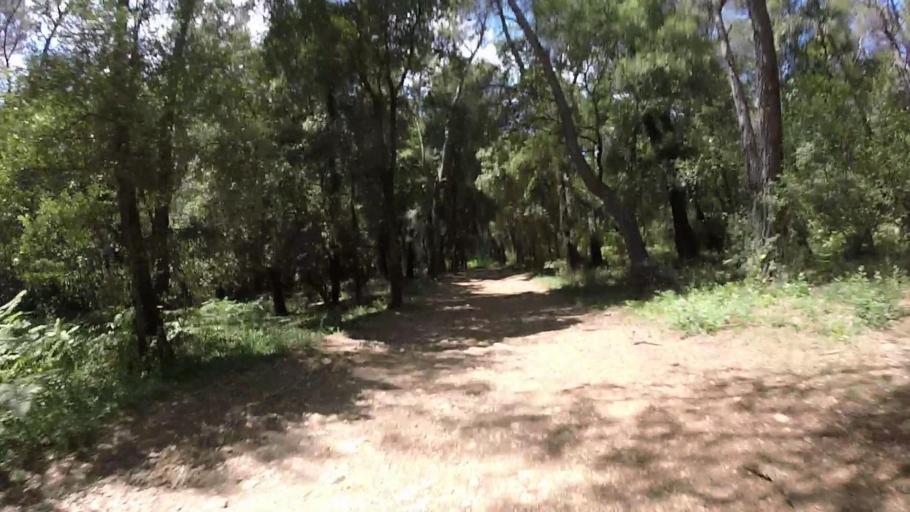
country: FR
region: Provence-Alpes-Cote d'Azur
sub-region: Departement des Alpes-Maritimes
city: Le Cannet
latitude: 43.5961
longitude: 7.0254
